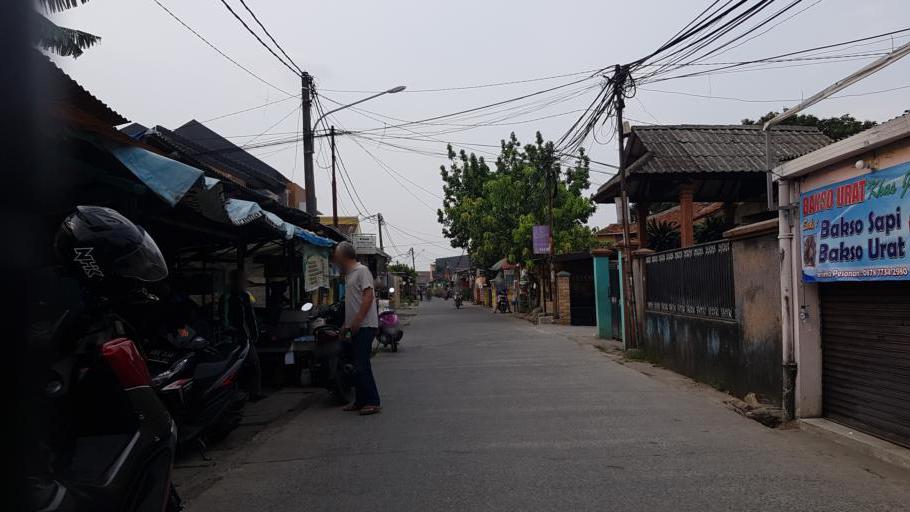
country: ID
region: West Java
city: Depok
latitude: -6.3936
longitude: 106.7977
